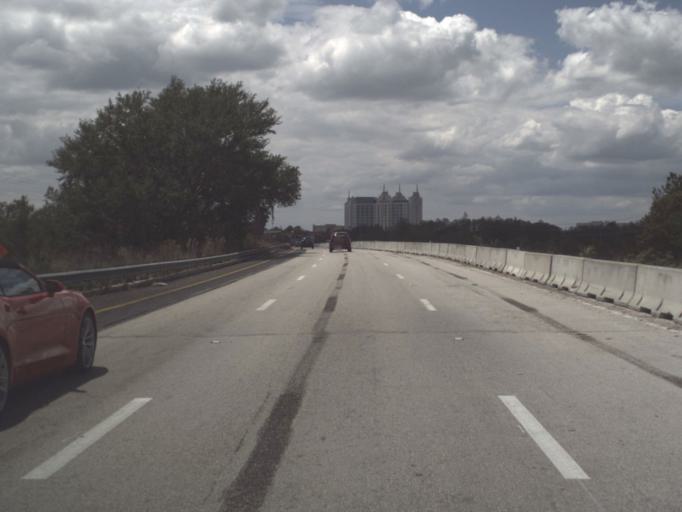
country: US
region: Florida
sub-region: Orange County
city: Tangelo Park
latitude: 28.4513
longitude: -81.4573
